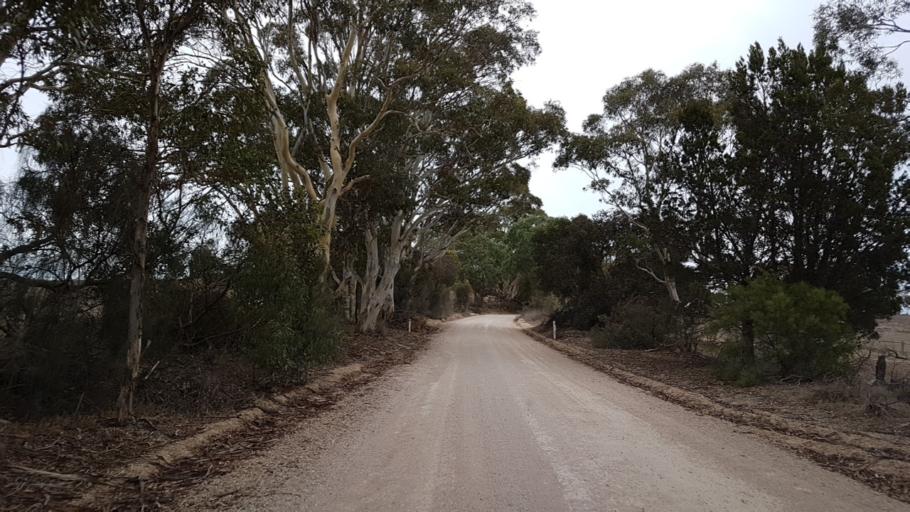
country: AU
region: South Australia
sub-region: Mount Barker
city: Nairne
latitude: -34.9985
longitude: 138.9864
